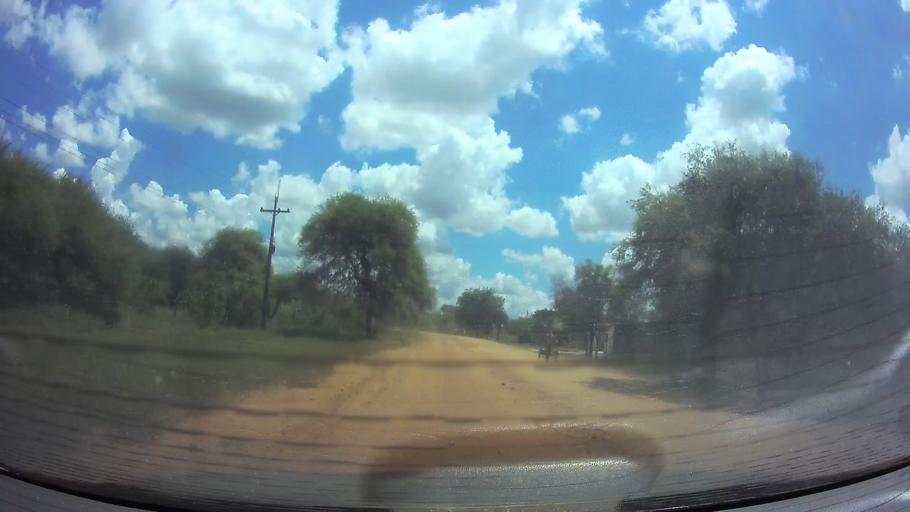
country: PY
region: Presidente Hayes
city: Nanawa
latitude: -25.2478
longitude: -57.6526
